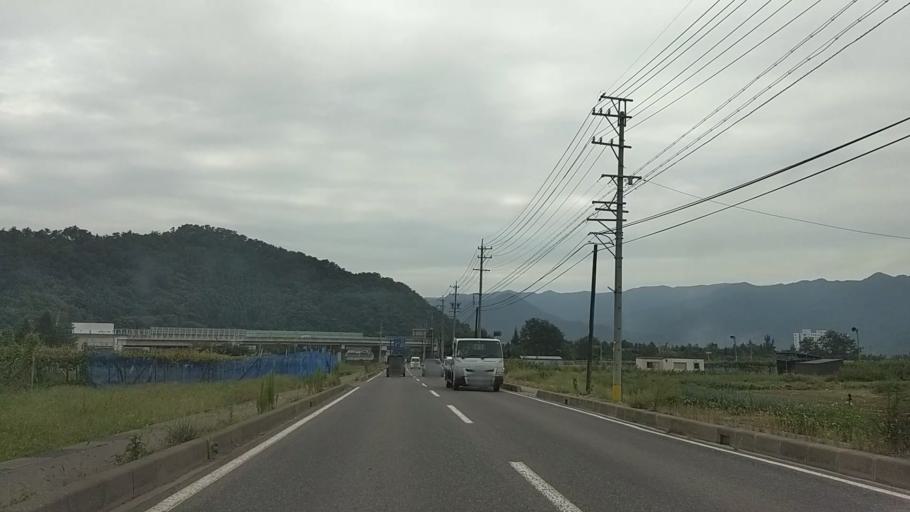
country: JP
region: Nagano
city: Nagano-shi
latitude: 36.5808
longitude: 138.2020
